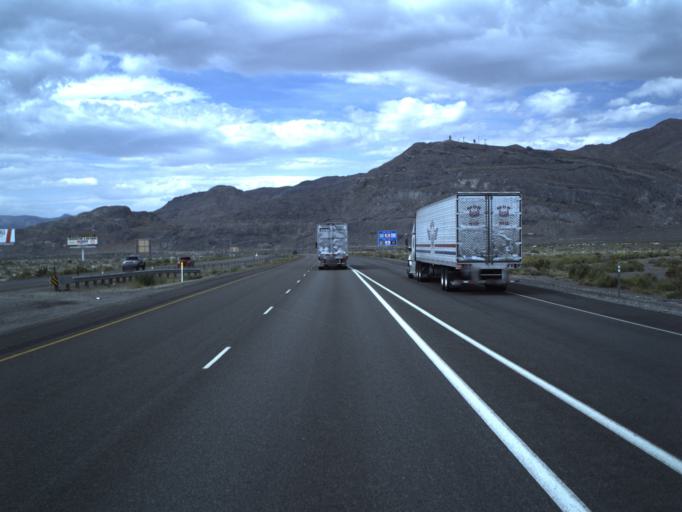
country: US
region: Utah
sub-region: Tooele County
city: Wendover
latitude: 40.7463
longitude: -113.9960
